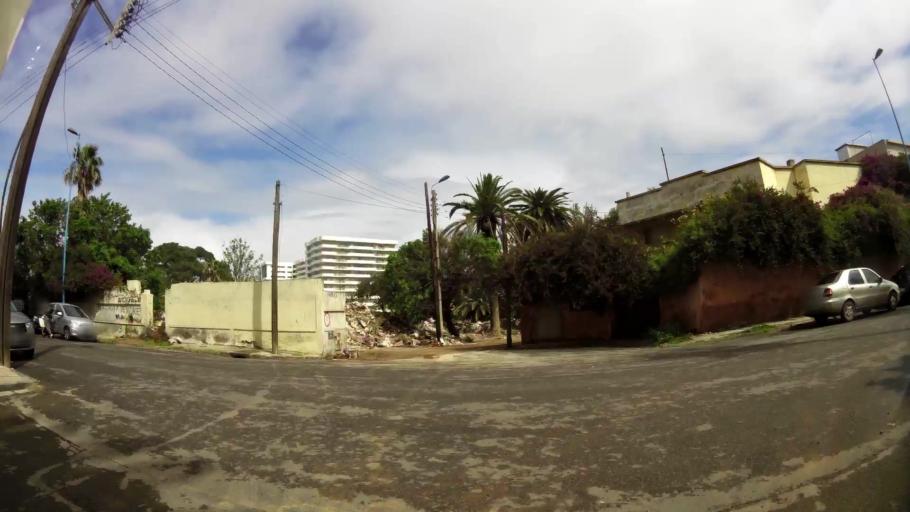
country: MA
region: Grand Casablanca
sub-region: Casablanca
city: Casablanca
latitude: 33.5790
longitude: -7.6316
